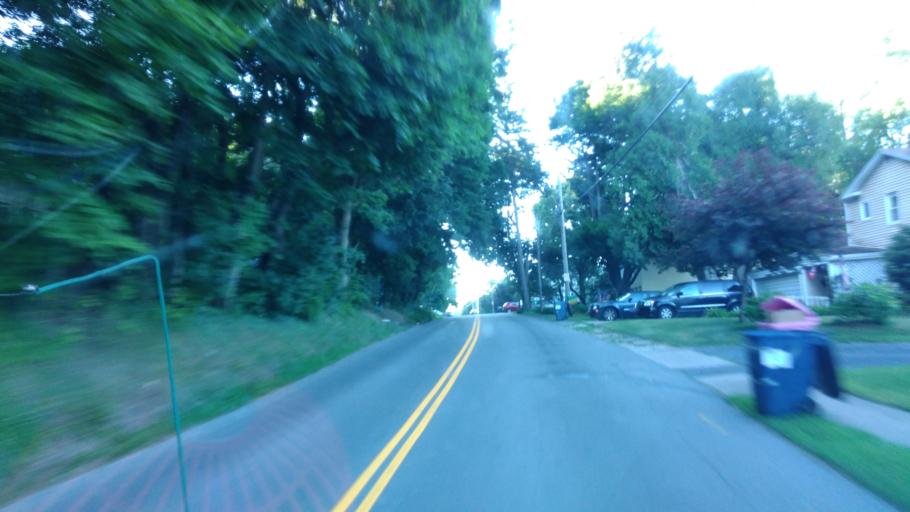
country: US
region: New York
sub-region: Wayne County
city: Lyons
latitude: 43.0664
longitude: -77.0022
